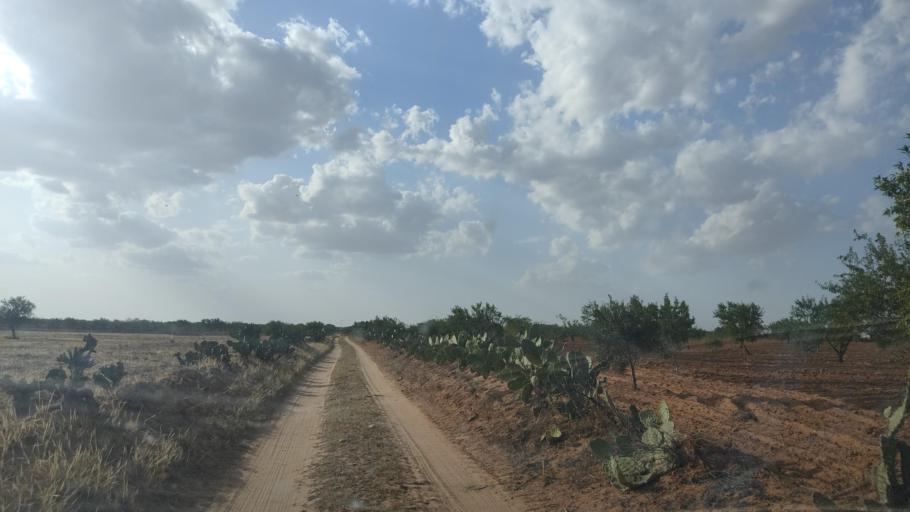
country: TN
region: Safaqis
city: Sfax
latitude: 34.8517
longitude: 10.5936
